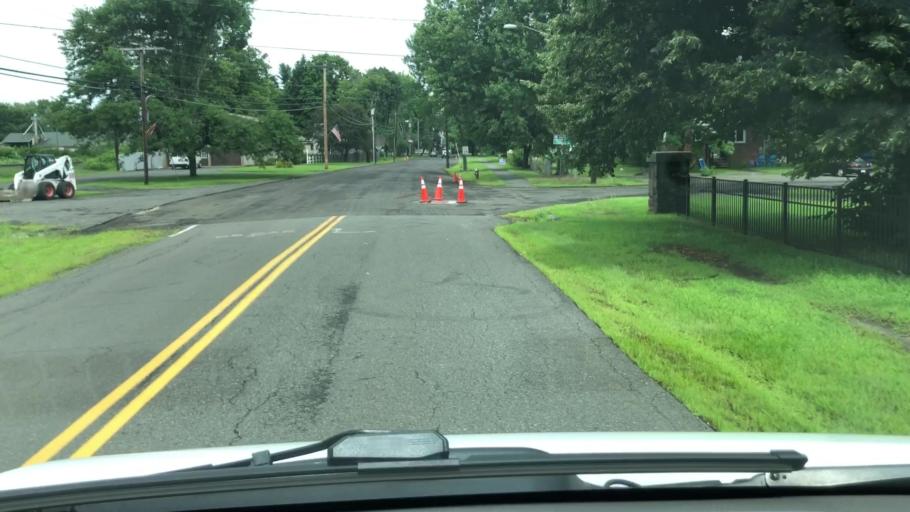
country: US
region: Massachusetts
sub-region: Franklin County
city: South Deerfield
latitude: 42.4722
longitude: -72.6111
